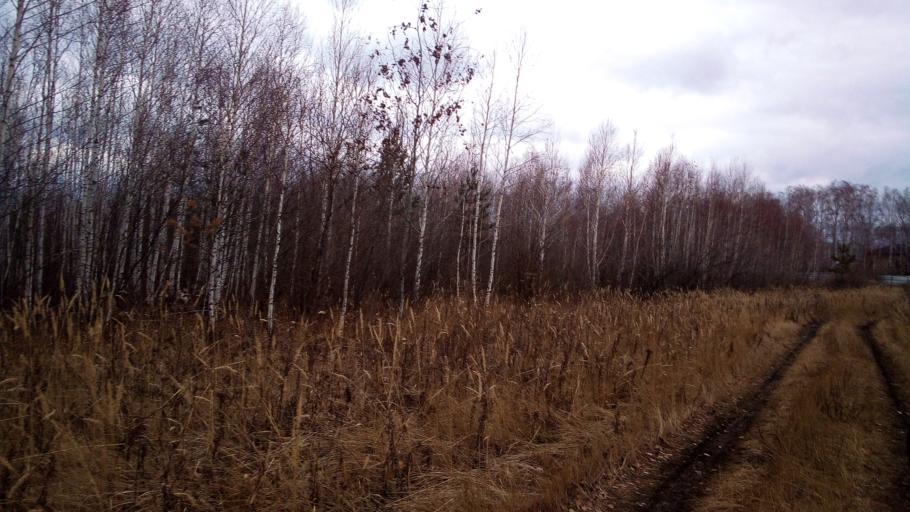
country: RU
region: Chelyabinsk
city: Sargazy
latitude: 55.1251
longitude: 61.2505
